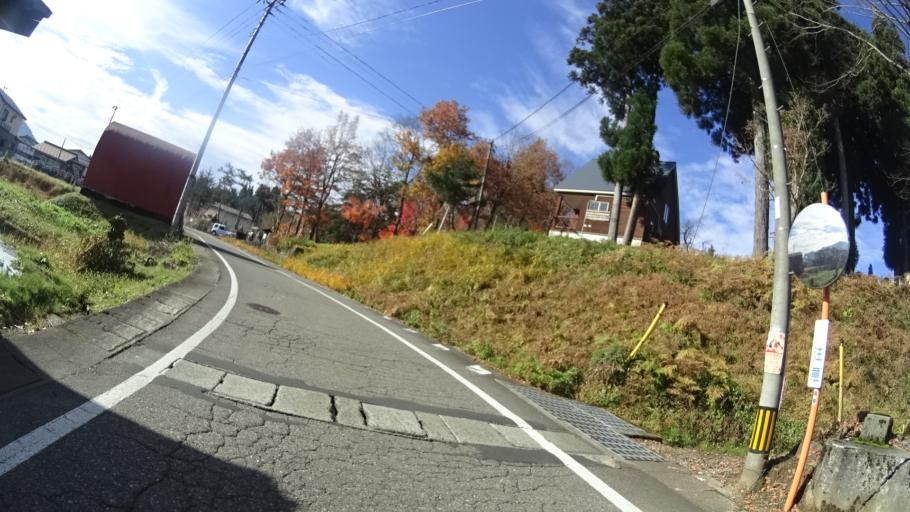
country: JP
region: Niigata
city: Tochio-honcho
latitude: 37.3220
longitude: 139.0169
